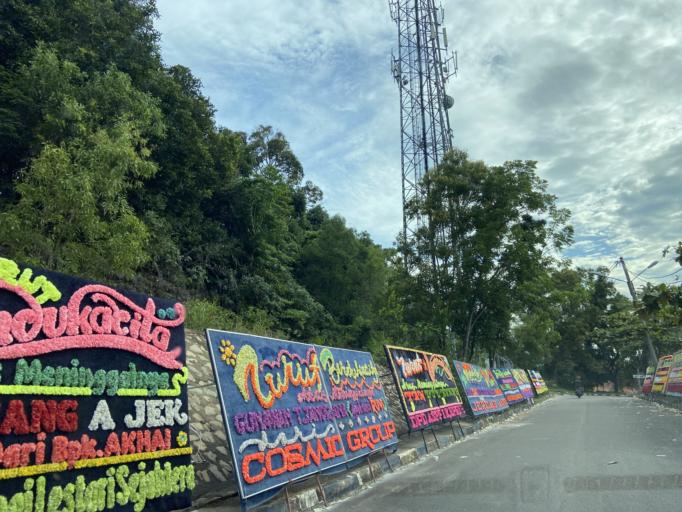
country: SG
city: Singapore
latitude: 1.1210
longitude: 104.0084
